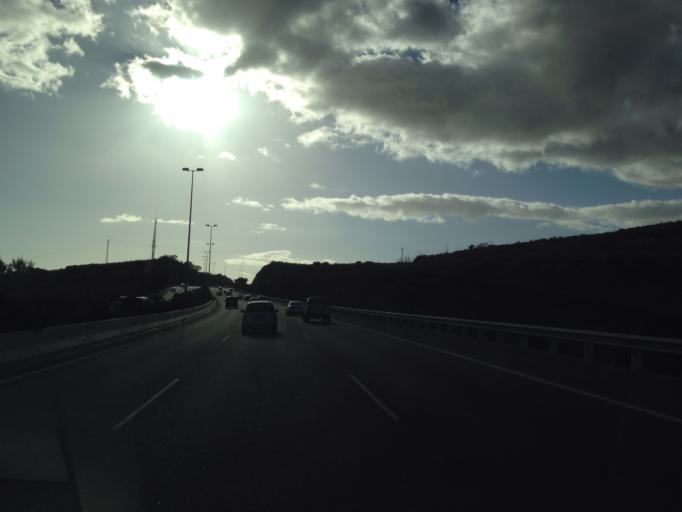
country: ES
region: Canary Islands
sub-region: Provincia de Las Palmas
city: Playa del Ingles
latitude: 27.7861
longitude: -15.5215
